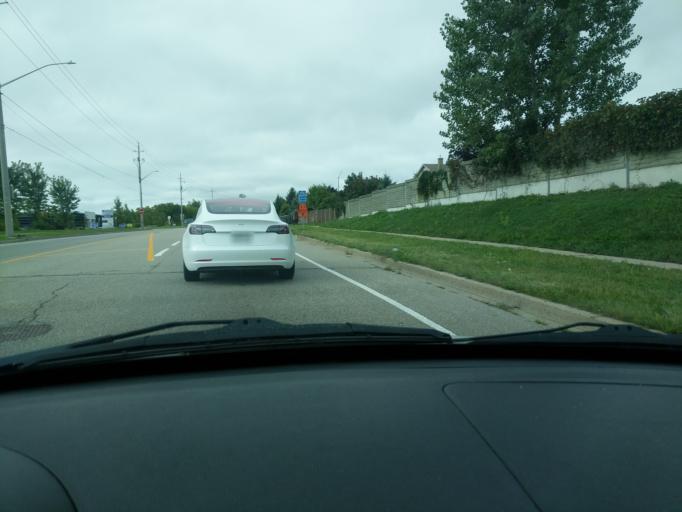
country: CA
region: Ontario
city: Cambridge
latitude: 43.4211
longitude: -80.2893
